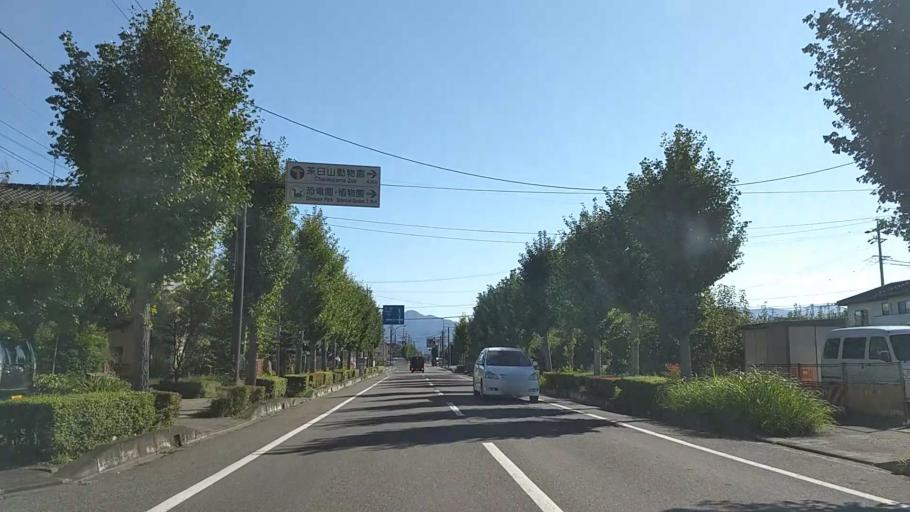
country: JP
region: Nagano
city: Nagano-shi
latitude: 36.5844
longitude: 138.1371
